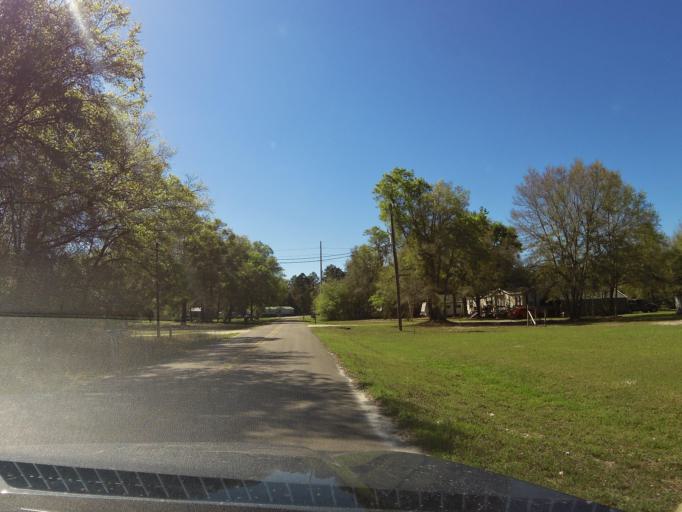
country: US
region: Florida
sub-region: Clay County
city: Keystone Heights
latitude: 29.8339
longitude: -82.0659
